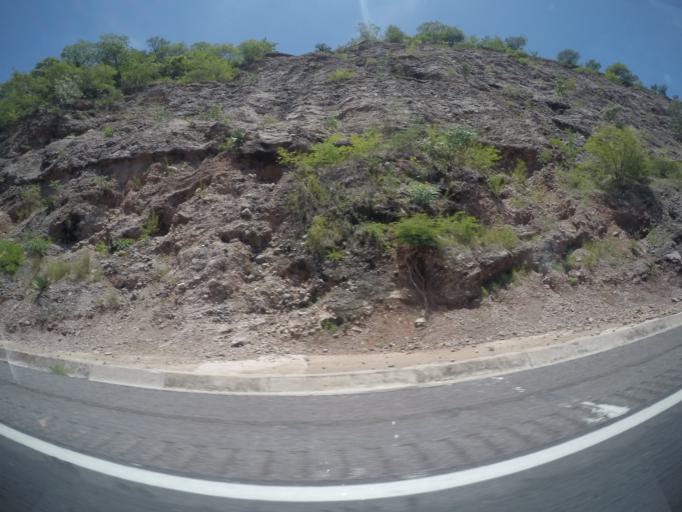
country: MX
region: Guerrero
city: Copalillo
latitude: 18.1190
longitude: -99.2065
